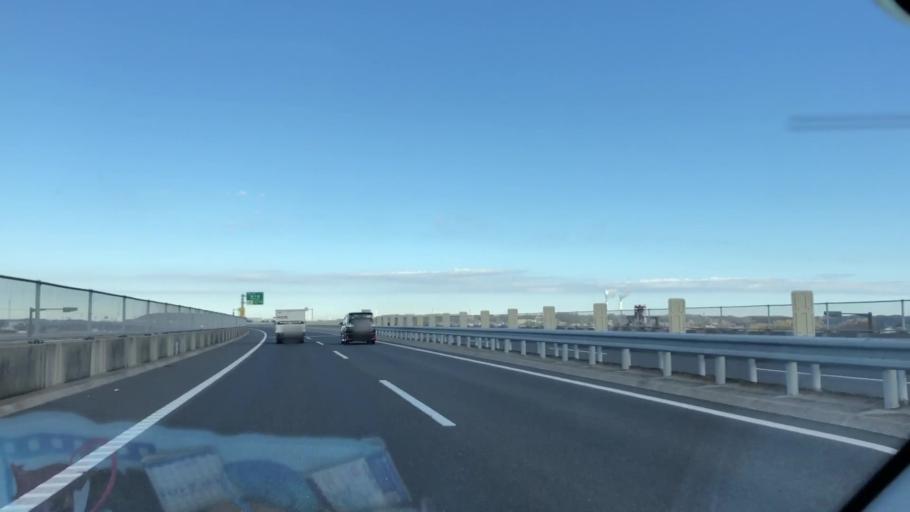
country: JP
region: Chiba
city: Kisarazu
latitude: 35.3997
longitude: 139.9673
